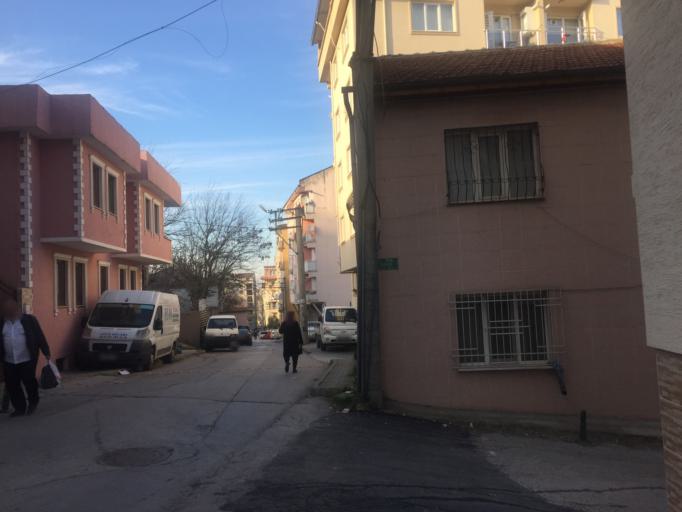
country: TR
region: Bursa
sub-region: Osmangazi
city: Bursa
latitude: 40.1878
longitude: 29.0837
